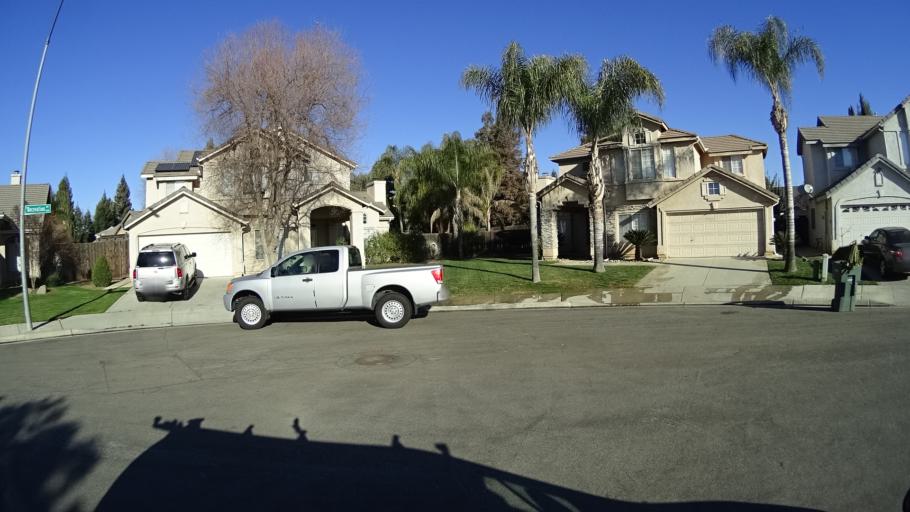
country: US
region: California
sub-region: Fresno County
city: Clovis
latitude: 36.8418
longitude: -119.7409
